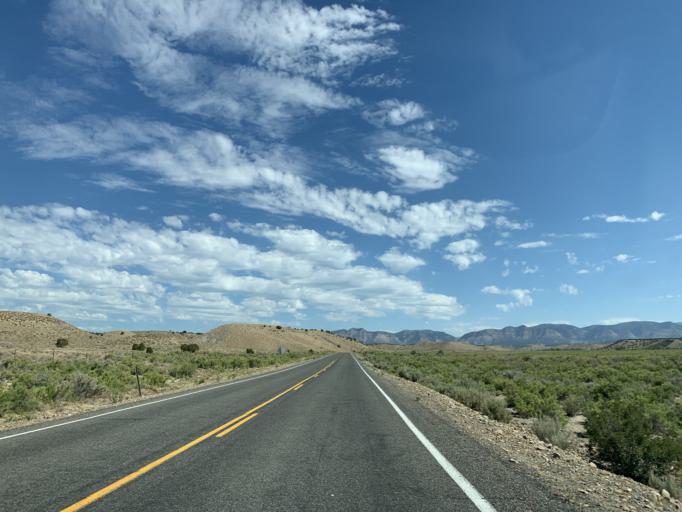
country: US
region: Utah
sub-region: Carbon County
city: Wellington
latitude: 39.5703
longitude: -110.6535
